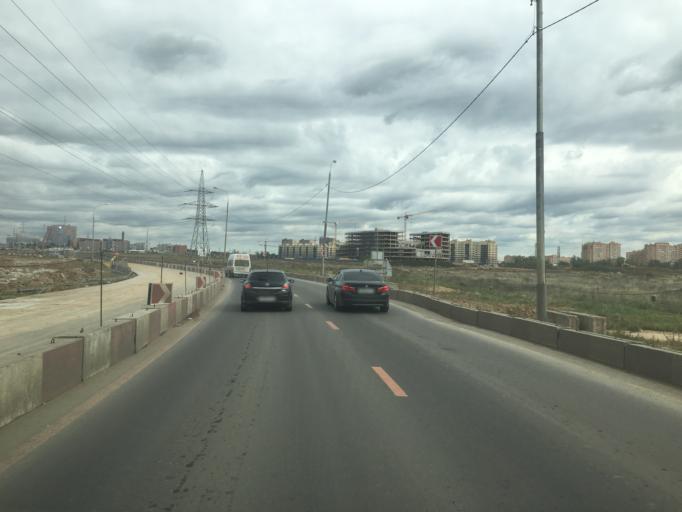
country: RU
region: Moskovskaya
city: Kommunarka
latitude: 55.5712
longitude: 37.4555
